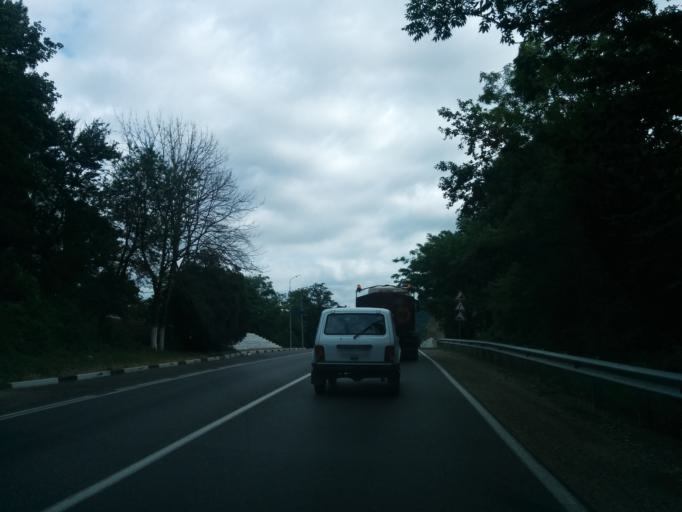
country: RU
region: Krasnodarskiy
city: Agoy
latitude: 44.1315
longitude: 39.0471
